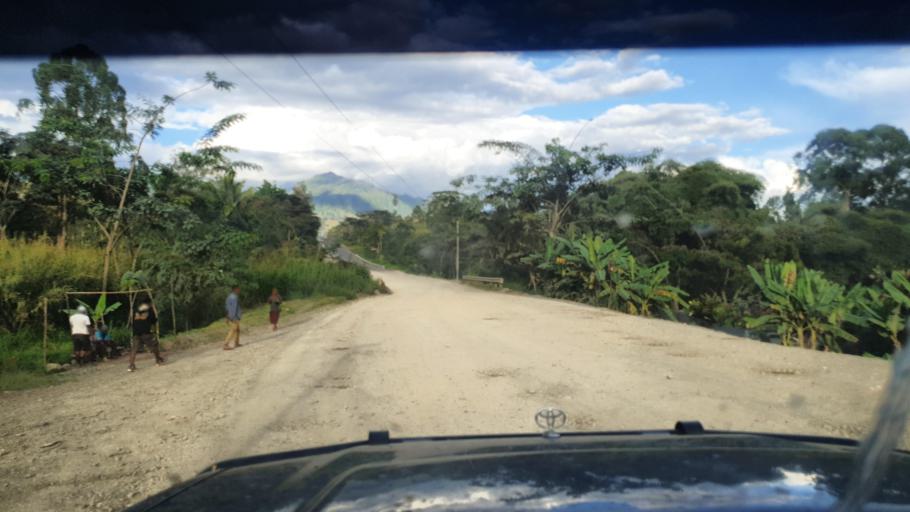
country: PG
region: Chimbu
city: Kundiawa
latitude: -5.9429
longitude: 144.8412
